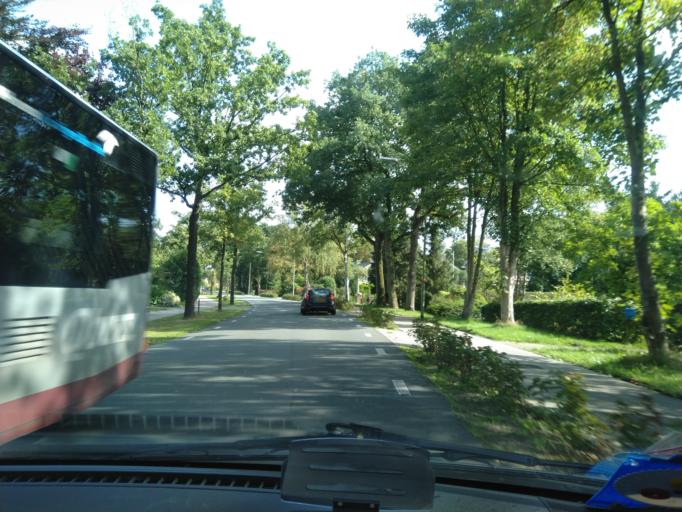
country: NL
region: Groningen
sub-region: Gemeente Groningen
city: Groningen
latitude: 53.1704
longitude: 6.5493
